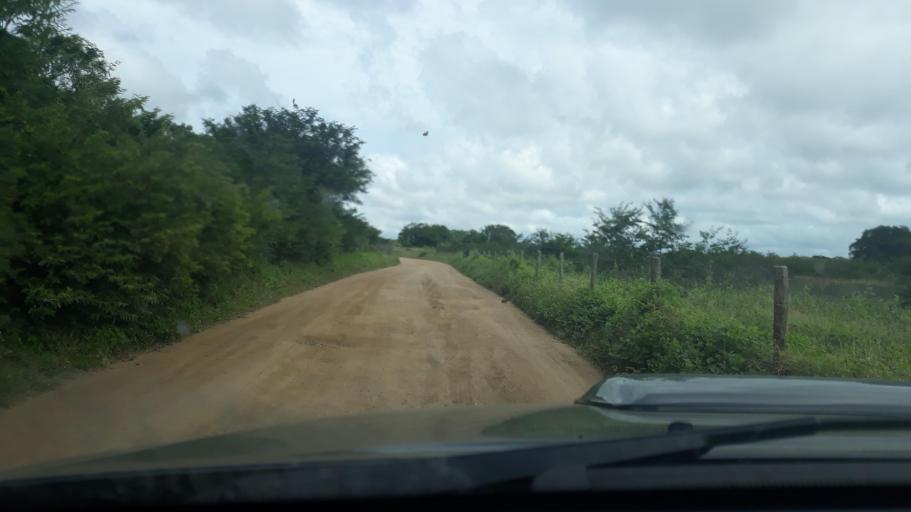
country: BR
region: Bahia
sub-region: Riacho De Santana
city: Riacho de Santana
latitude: -13.9110
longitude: -42.9497
